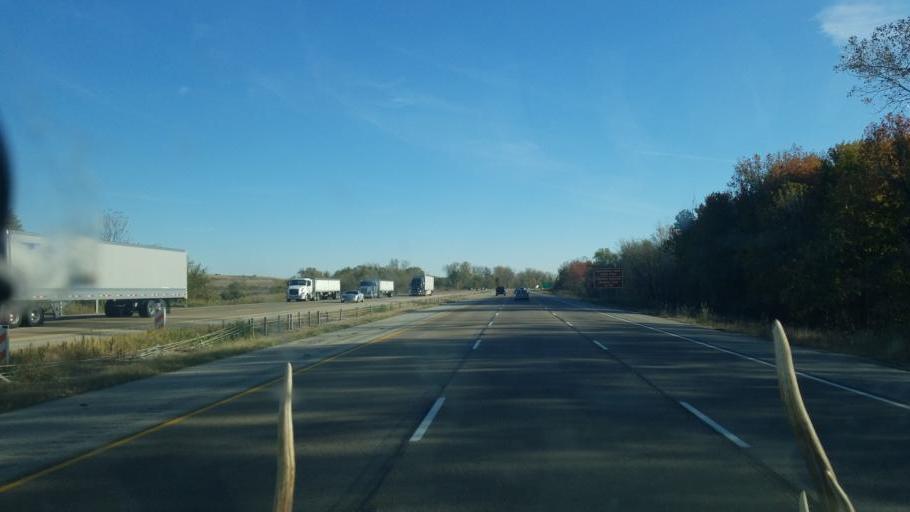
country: US
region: Illinois
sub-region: Saint Clair County
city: Fairmont City
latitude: 38.6568
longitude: -90.1115
